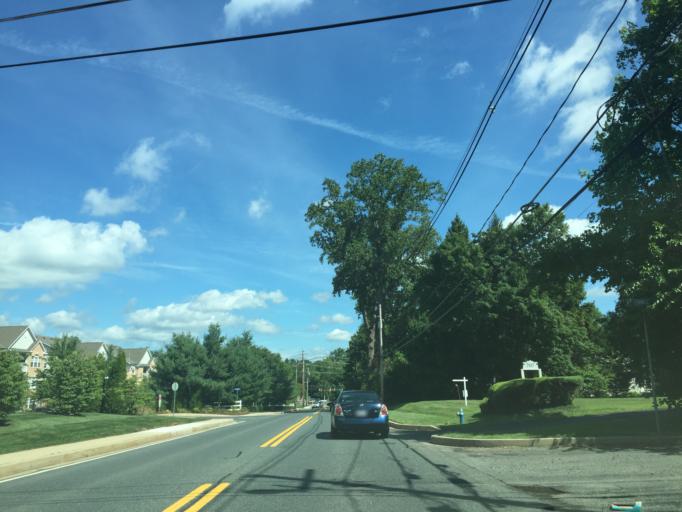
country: US
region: Maryland
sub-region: Harford County
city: North Bel Air
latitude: 39.5458
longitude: -76.3495
